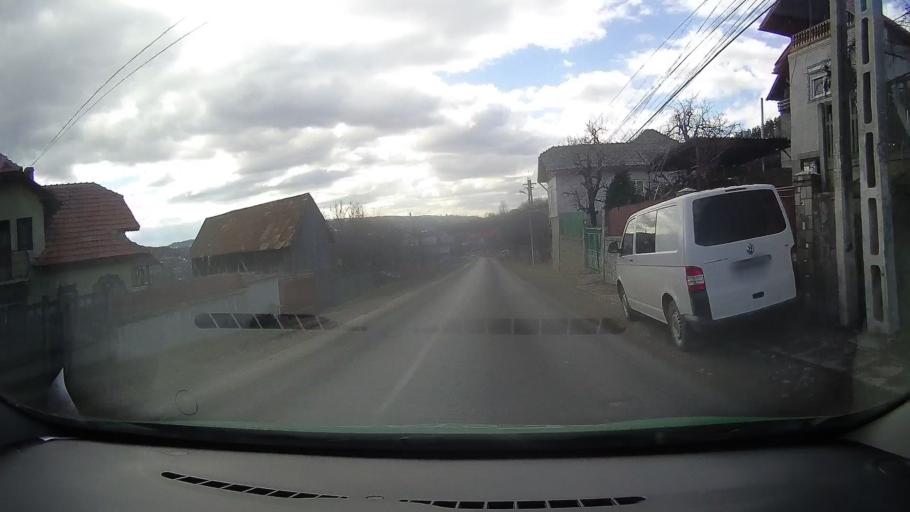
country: RO
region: Dambovita
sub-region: Comuna Buciumeni
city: Dealu Mare
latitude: 45.1602
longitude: 25.4474
